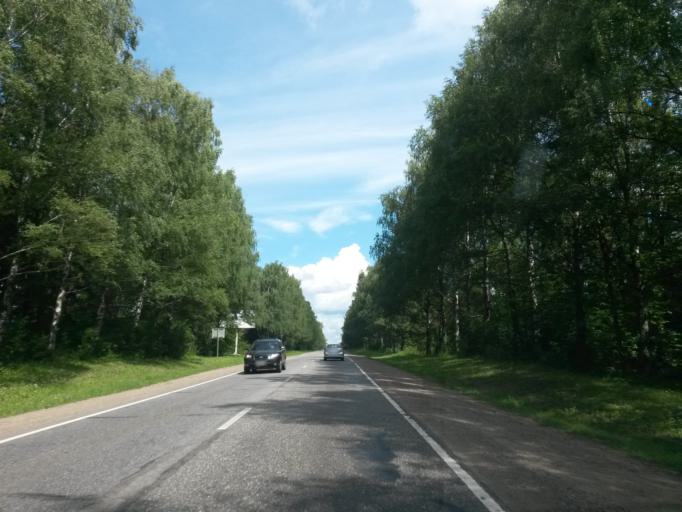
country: RU
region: Jaroslavl
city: Pereslavl'-Zalesskiy
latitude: 56.7868
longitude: 38.8852
